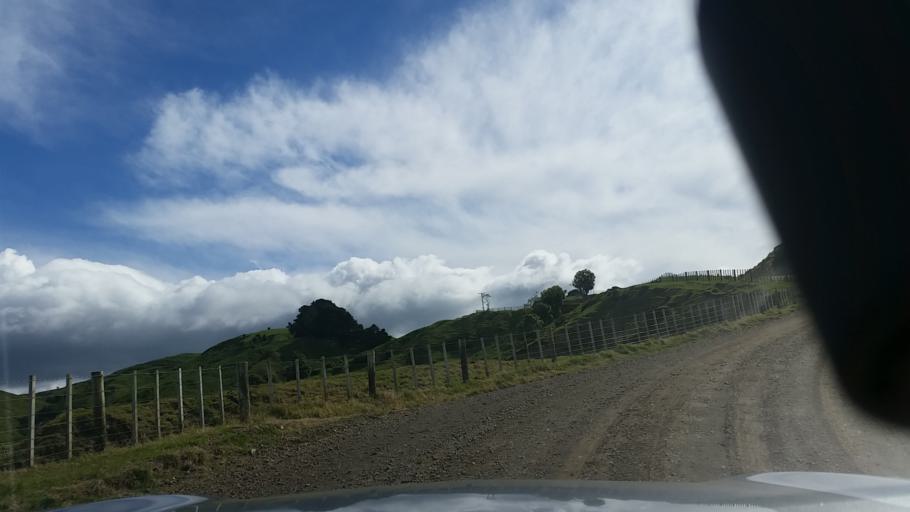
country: NZ
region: Hawke's Bay
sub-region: Napier City
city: Napier
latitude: -39.2161
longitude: 176.9725
